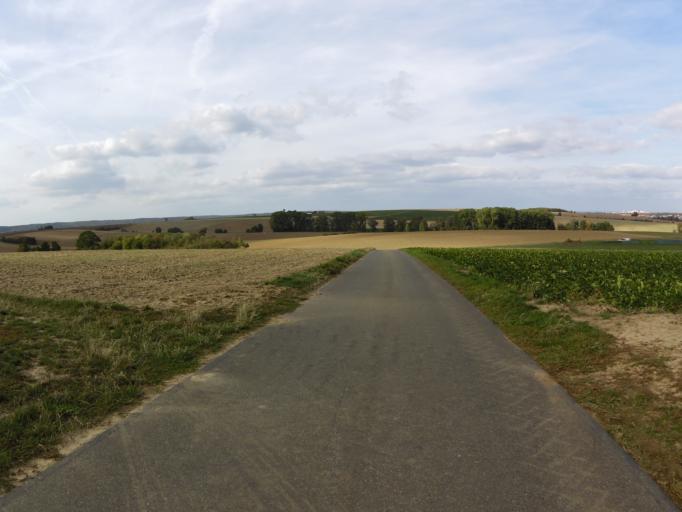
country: DE
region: Bavaria
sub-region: Regierungsbezirk Unterfranken
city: Eibelstadt
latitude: 49.7017
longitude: 9.9563
